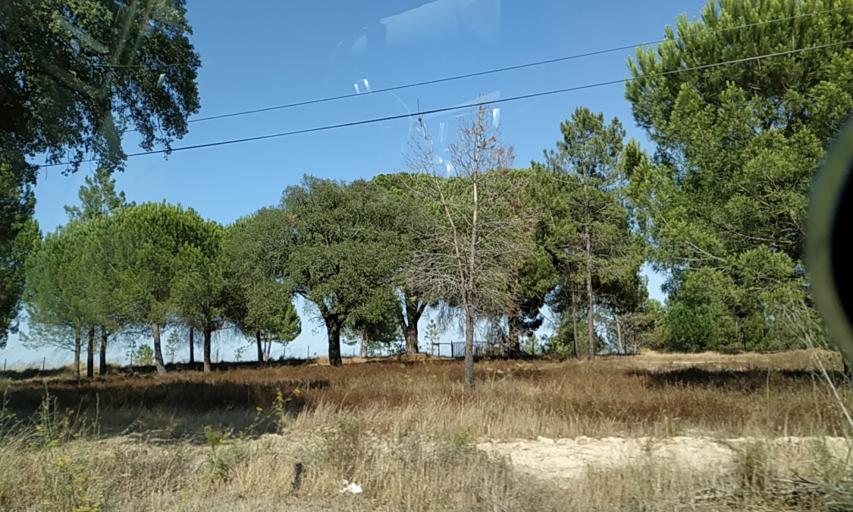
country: PT
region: Santarem
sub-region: Benavente
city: Poceirao
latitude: 38.7547
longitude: -8.6321
